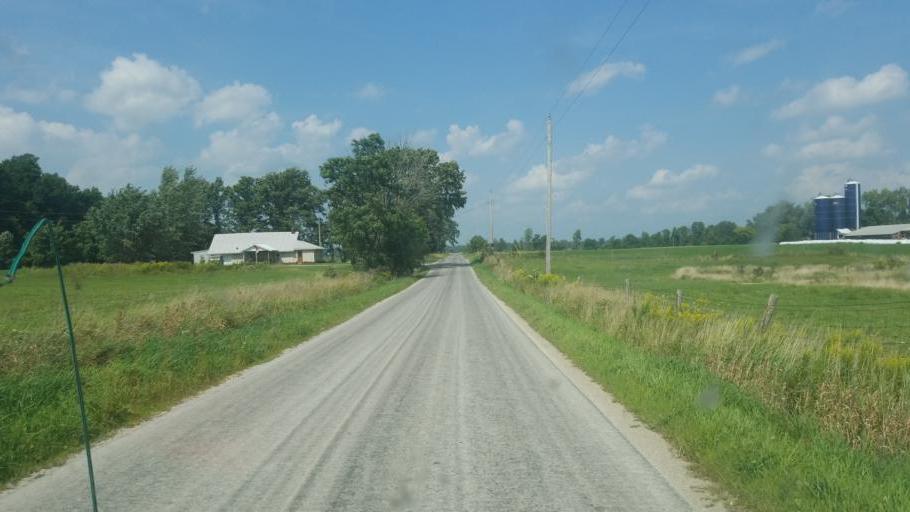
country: US
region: Ohio
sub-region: Huron County
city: Greenwich
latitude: 40.9630
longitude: -82.4316
